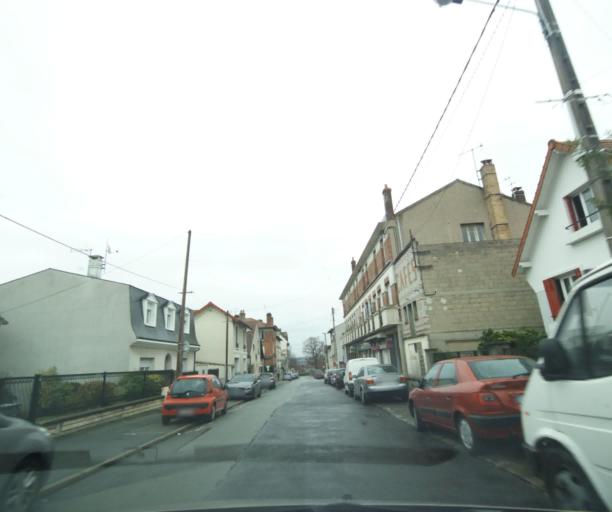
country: FR
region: Ile-de-France
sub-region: Departement du Val-de-Marne
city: Villeneuve-le-Roi
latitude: 48.7346
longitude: 2.4144
